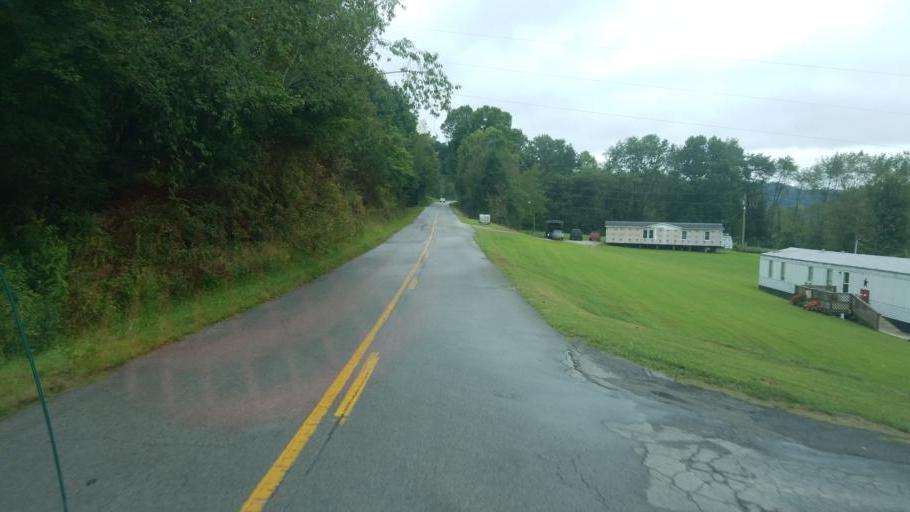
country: US
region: Kentucky
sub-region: Rowan County
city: Morehead
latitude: 38.3592
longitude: -83.5334
